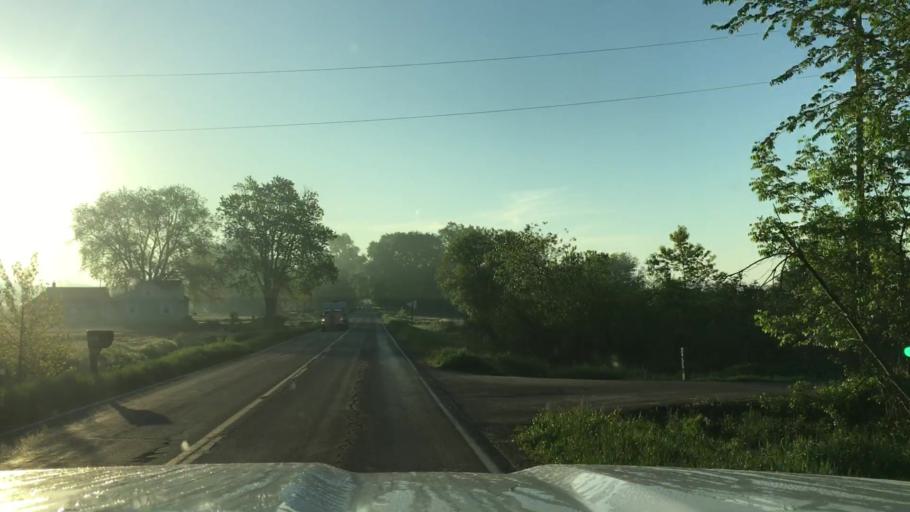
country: US
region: Michigan
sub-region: Kent County
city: Byron Center
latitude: 42.7829
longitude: -85.7358
